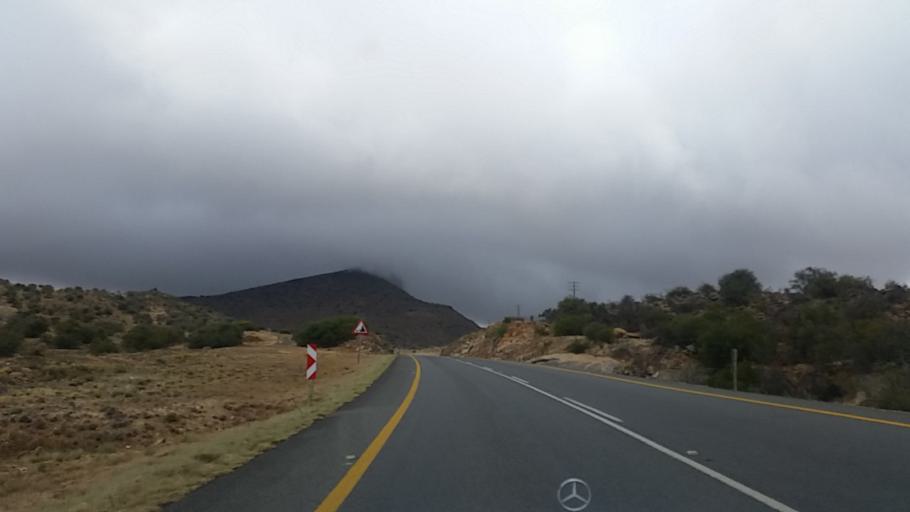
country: ZA
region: Eastern Cape
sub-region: Cacadu District Municipality
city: Graaff-Reinet
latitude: -32.1065
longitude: 24.6067
